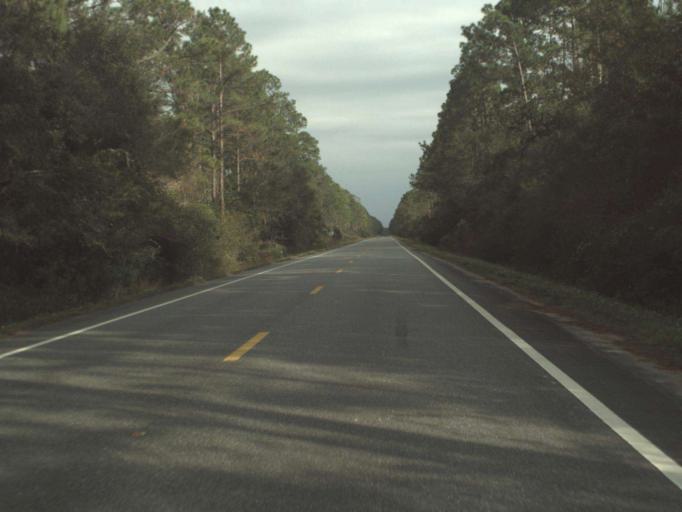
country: US
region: Florida
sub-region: Franklin County
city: Apalachicola
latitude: 29.8449
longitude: -84.9625
